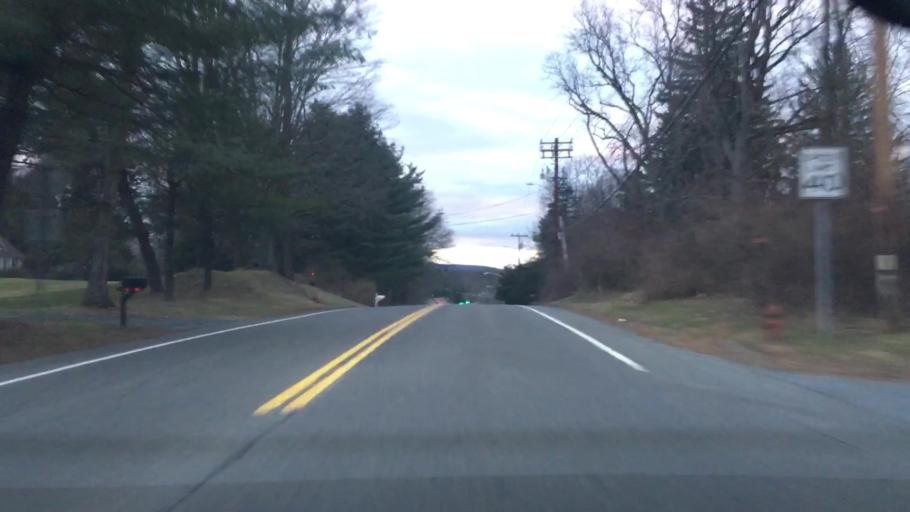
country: US
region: New York
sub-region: Dutchess County
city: Arlington
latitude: 41.6778
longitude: -73.8869
